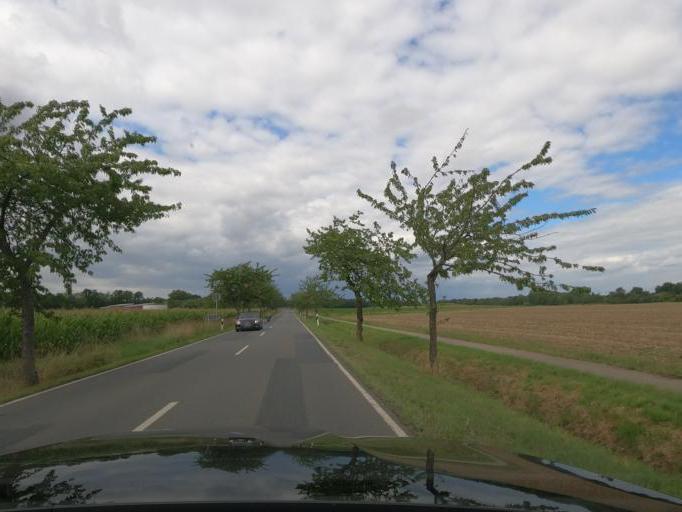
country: DE
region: Lower Saxony
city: Algermissen
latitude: 52.2629
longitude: 9.9618
